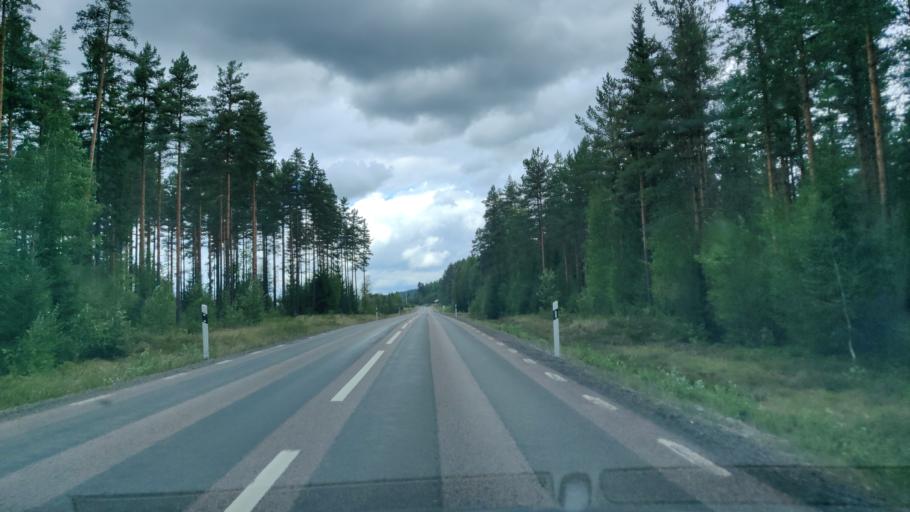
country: SE
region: Vaermland
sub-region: Torsby Kommun
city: Torsby
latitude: 60.5352
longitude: 13.1227
